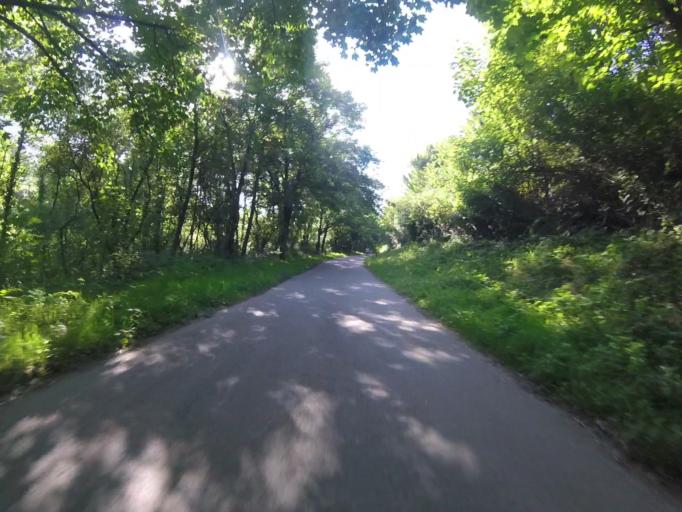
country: ES
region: Basque Country
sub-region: Provincia de Guipuzcoa
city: Pasaia
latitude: 43.3071
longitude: -1.9268
